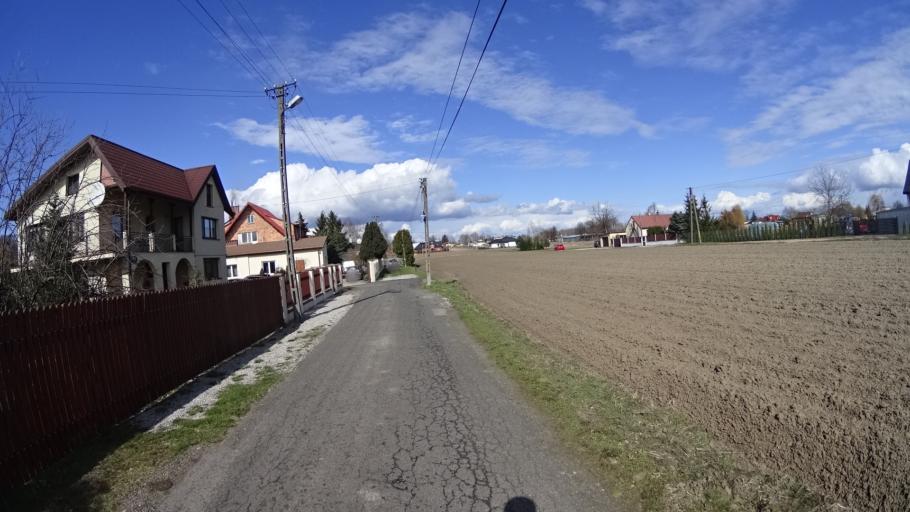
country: PL
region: Masovian Voivodeship
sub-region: Powiat warszawski zachodni
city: Jozefow
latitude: 52.2078
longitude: 20.6937
